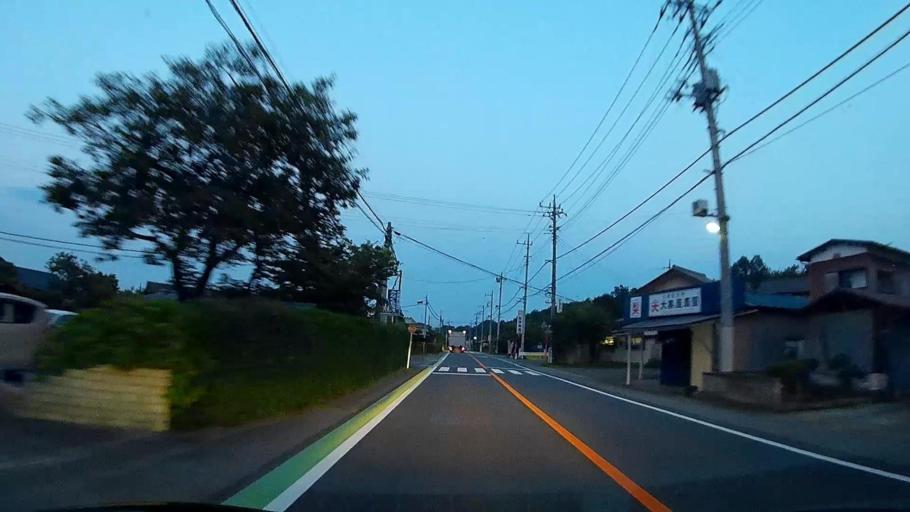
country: JP
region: Gunma
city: Annaka
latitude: 36.3542
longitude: 138.9311
